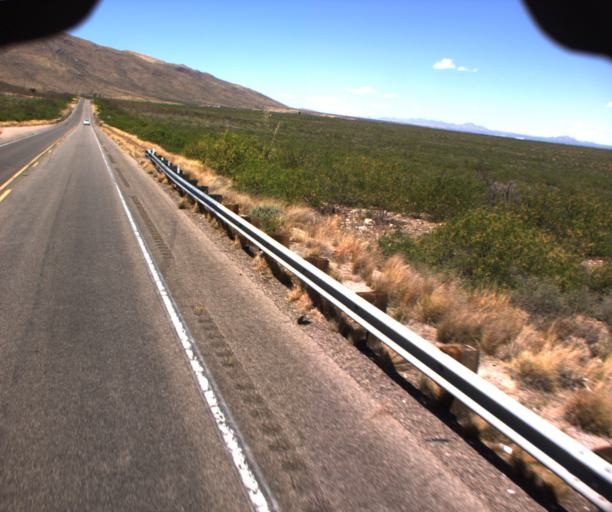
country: US
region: Arizona
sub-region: Cochise County
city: Bisbee
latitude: 31.4292
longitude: -109.8086
